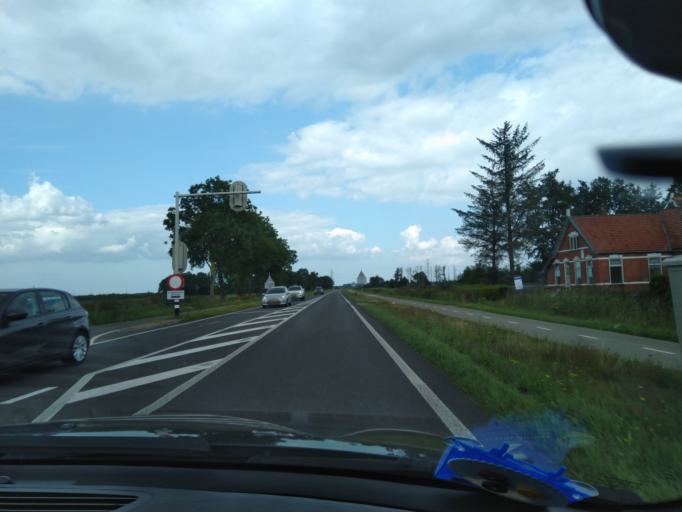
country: NL
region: Groningen
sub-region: Gemeente Groningen
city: Groningen
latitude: 53.1677
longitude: 6.4966
